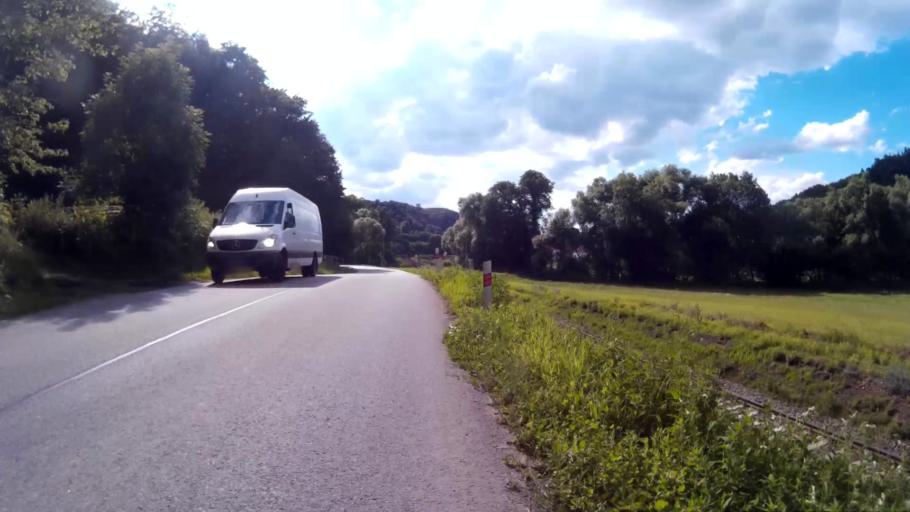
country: CZ
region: South Moravian
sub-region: Okres Brno-Venkov
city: Rosice
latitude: 49.1639
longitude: 16.4296
